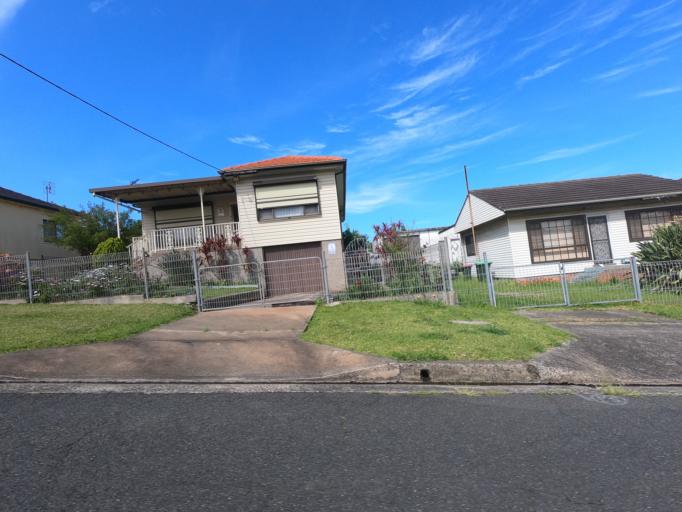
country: AU
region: New South Wales
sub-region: Wollongong
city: Lake Heights
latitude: -34.4818
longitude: 150.8691
